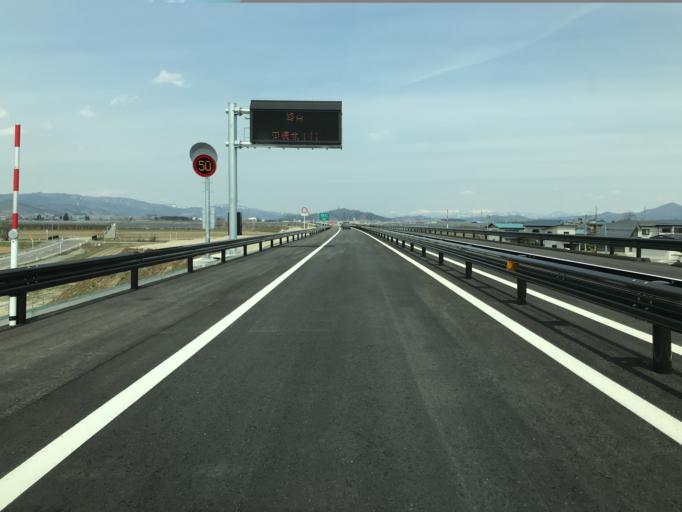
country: JP
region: Yamagata
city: Higashine
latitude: 38.4400
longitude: 140.3538
